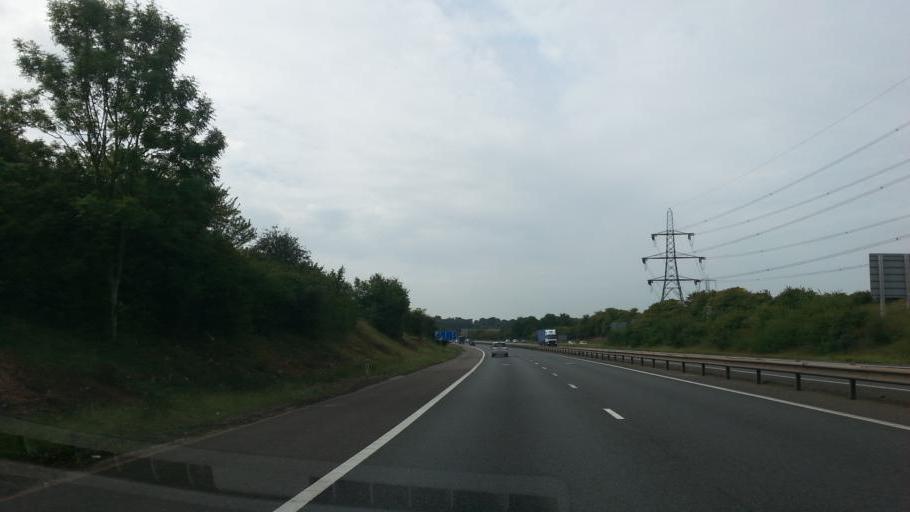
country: GB
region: England
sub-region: Hertfordshire
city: Letchworth Garden City
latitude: 51.9627
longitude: -0.2046
